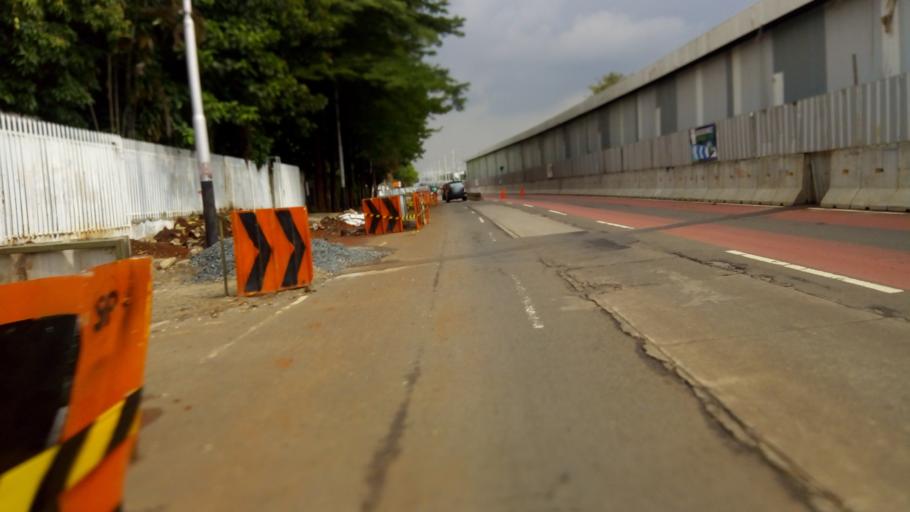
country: ID
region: Jakarta Raya
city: Jakarta
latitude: -6.2319
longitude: 106.7986
